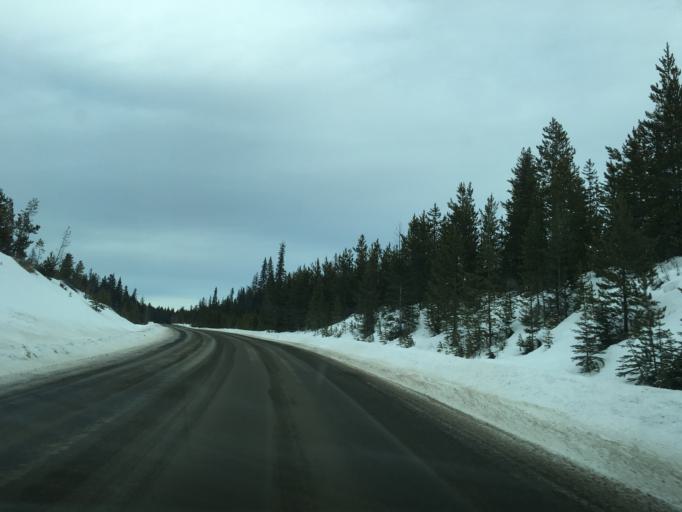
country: CA
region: British Columbia
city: Kamloops
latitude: 50.5202
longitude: -120.4741
